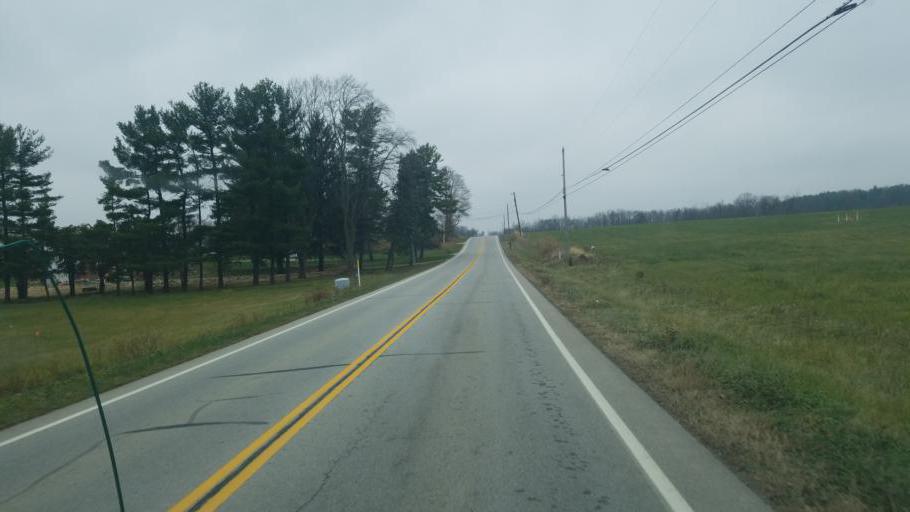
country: US
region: Ohio
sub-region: Medina County
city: Medina
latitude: 41.1429
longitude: -81.9236
